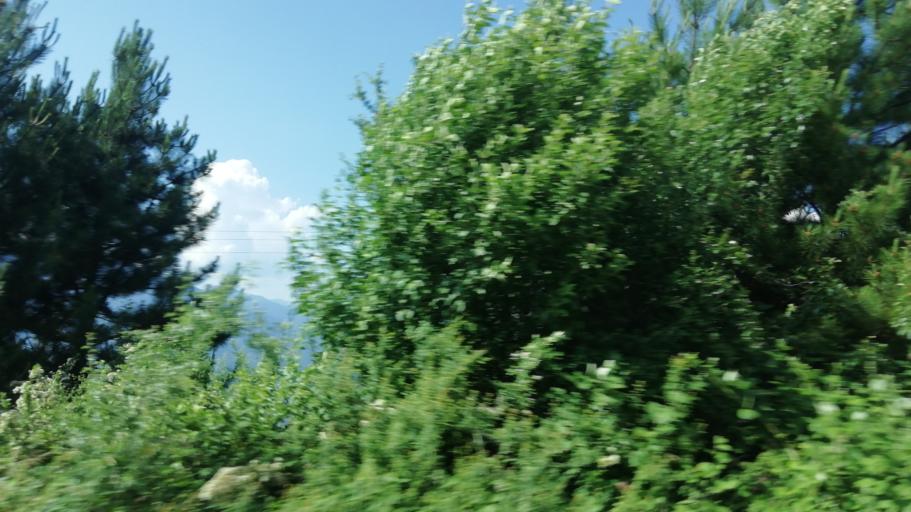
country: TR
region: Karabuk
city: Karabuk
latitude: 41.1246
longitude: 32.5833
